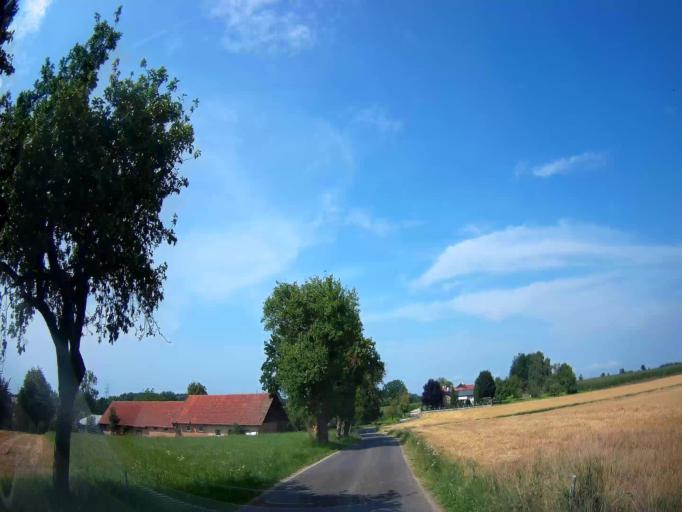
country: AT
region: Upper Austria
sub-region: Politischer Bezirk Kirchdorf an der Krems
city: Kremsmunster
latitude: 48.0764
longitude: 14.0984
